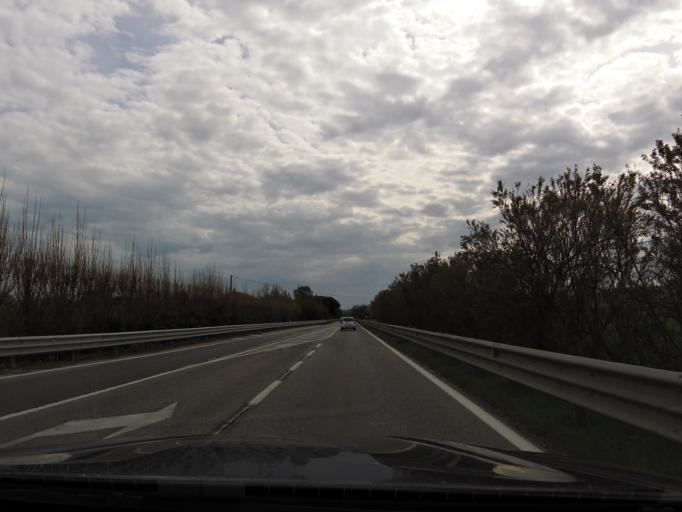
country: IT
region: The Marches
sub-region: Provincia di Macerata
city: Porto Recanati
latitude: 43.3985
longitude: 13.6788
